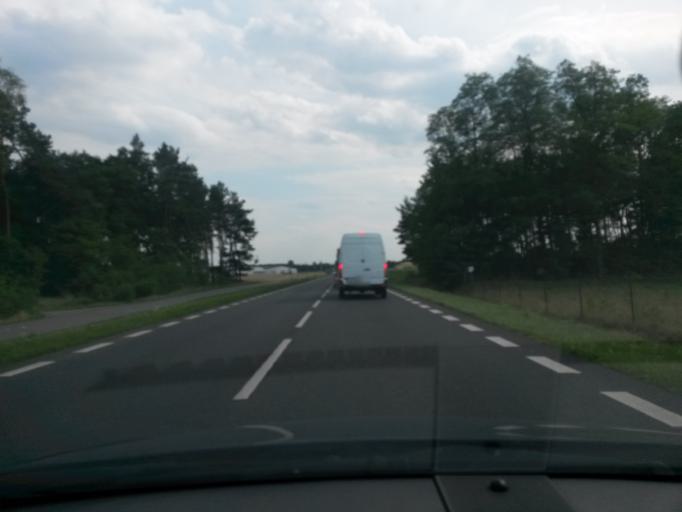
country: PL
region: Greater Poland Voivodeship
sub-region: Powiat sremski
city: Srem
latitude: 52.1152
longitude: 17.0436
